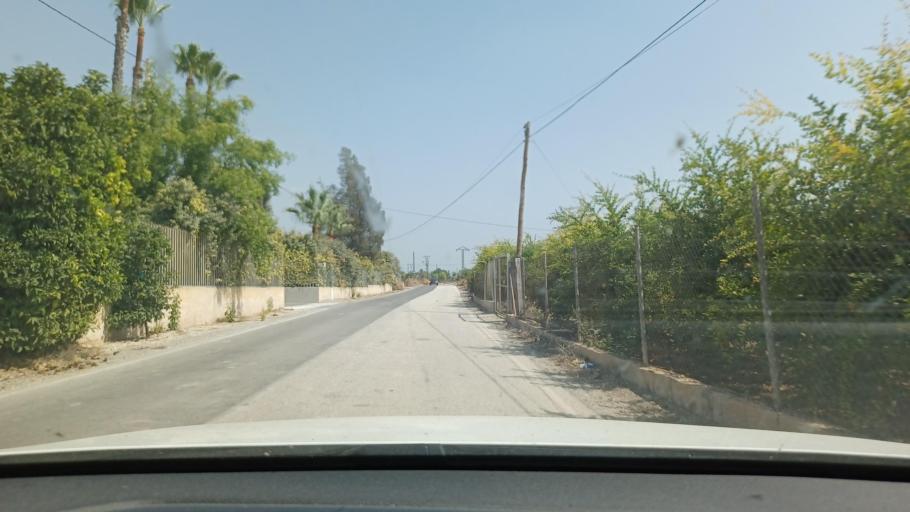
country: ES
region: Valencia
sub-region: Provincia de Alicante
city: Elche
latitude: 38.2392
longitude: -0.6922
